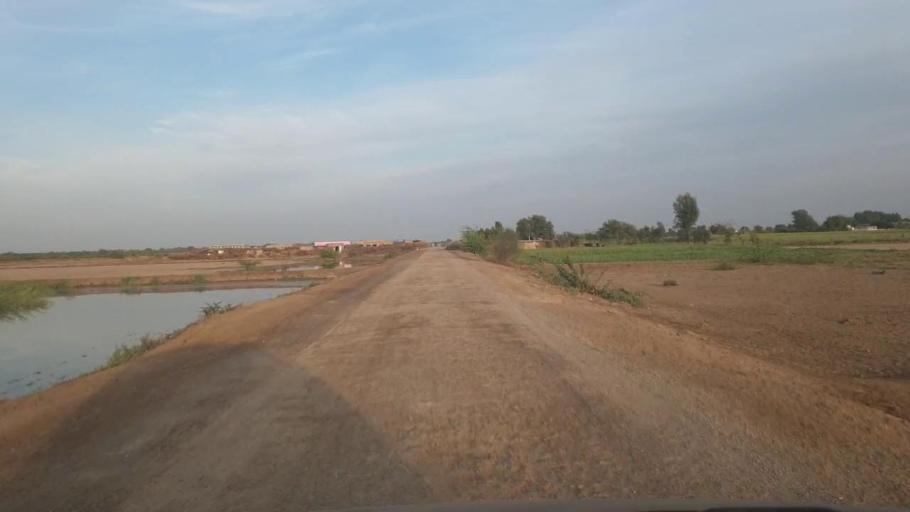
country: PK
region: Sindh
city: Kunri
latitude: 25.2269
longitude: 69.5494
